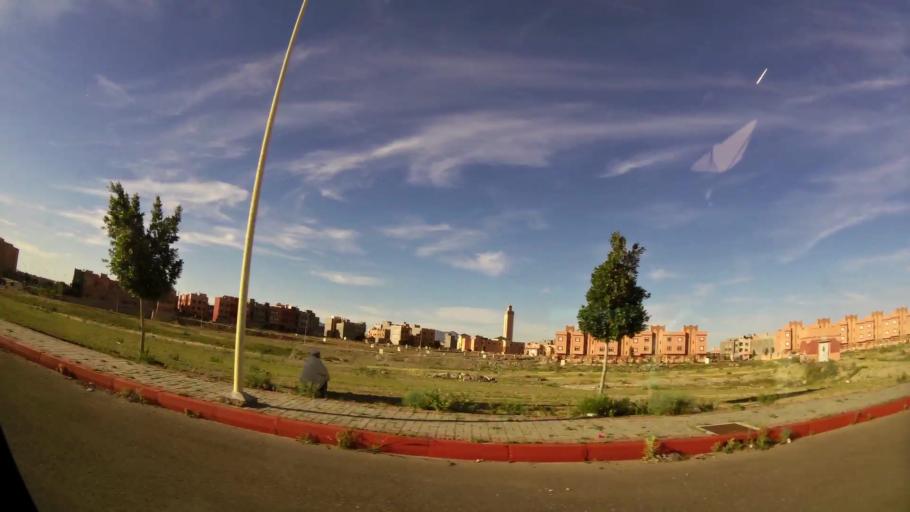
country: MA
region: Marrakech-Tensift-Al Haouz
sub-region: Marrakech
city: Marrakesh
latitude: 31.7542
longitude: -8.1004
